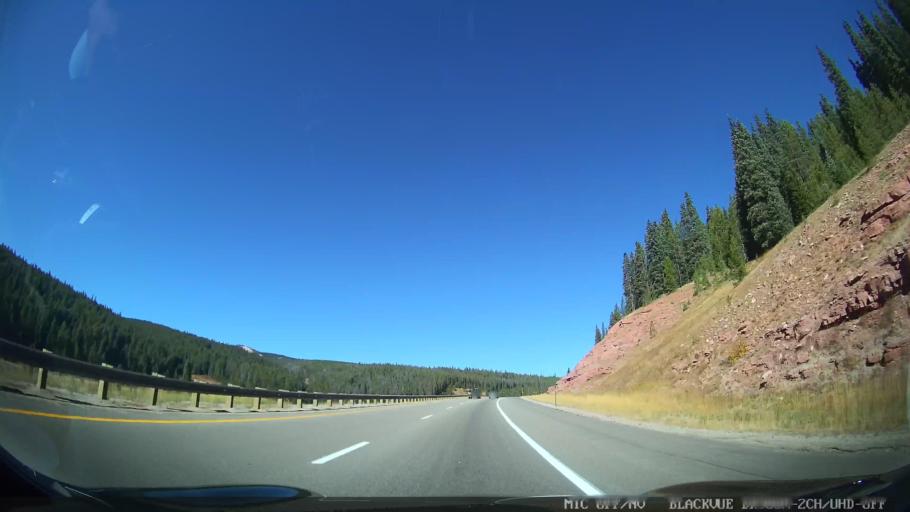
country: US
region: Colorado
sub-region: Summit County
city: Frisco
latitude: 39.5064
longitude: -106.1969
